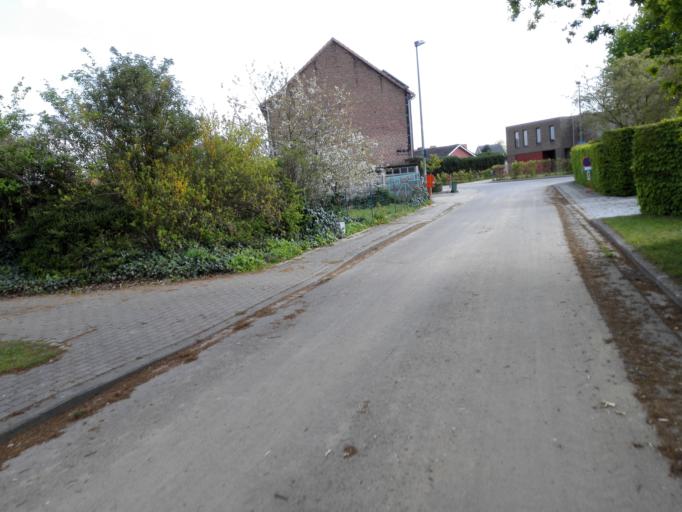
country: BE
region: Flanders
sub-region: Provincie Vlaams-Brabant
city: Rotselaar
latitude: 50.9292
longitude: 4.7190
